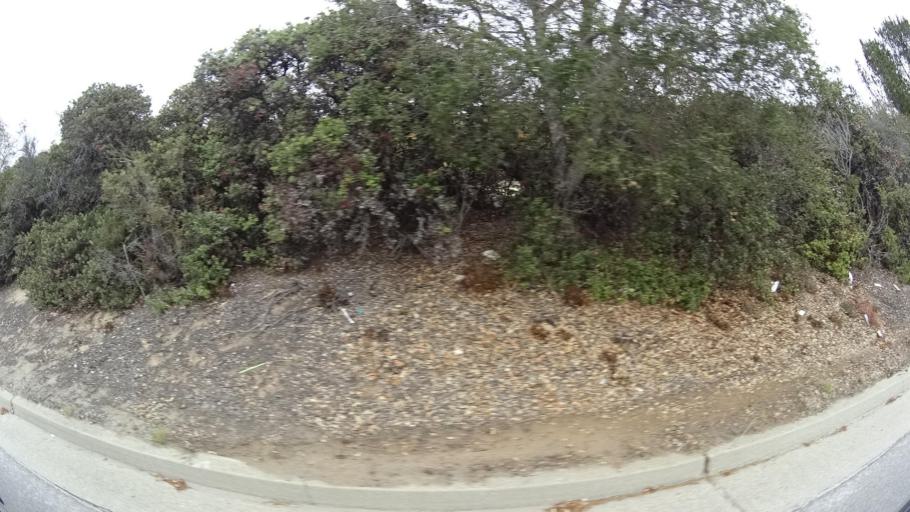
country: US
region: California
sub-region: Monterey County
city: Del Rey Oaks
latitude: 36.5782
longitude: -121.8123
